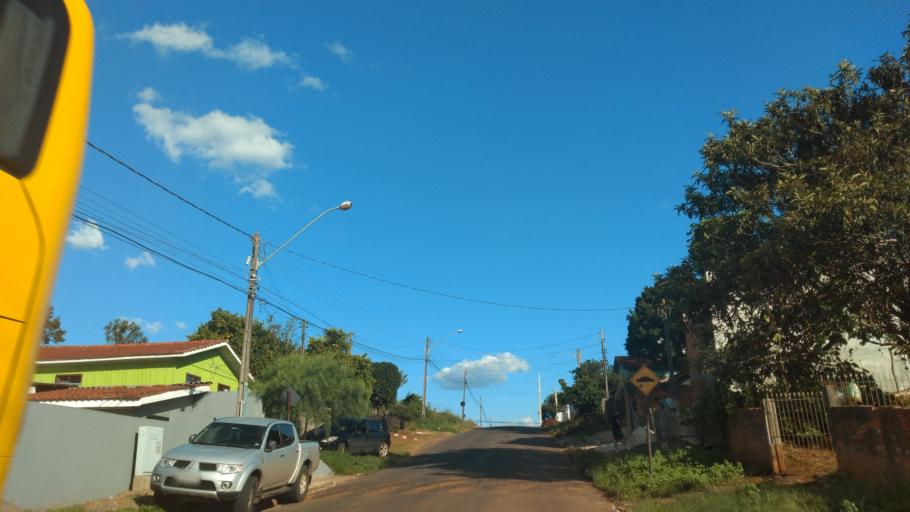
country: BR
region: Parana
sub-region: Guarapuava
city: Guarapuava
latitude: -25.4004
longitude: -51.4809
